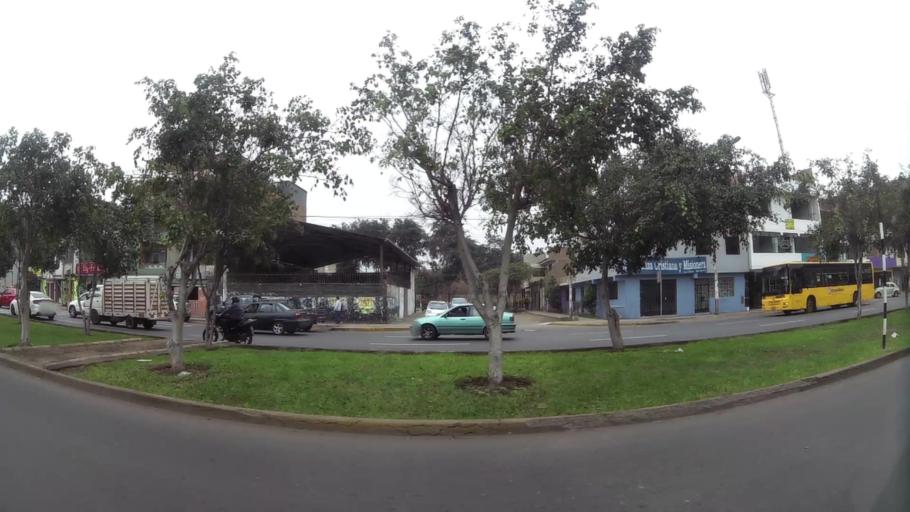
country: PE
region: Lima
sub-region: Lima
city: Independencia
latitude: -11.9397
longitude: -77.0776
